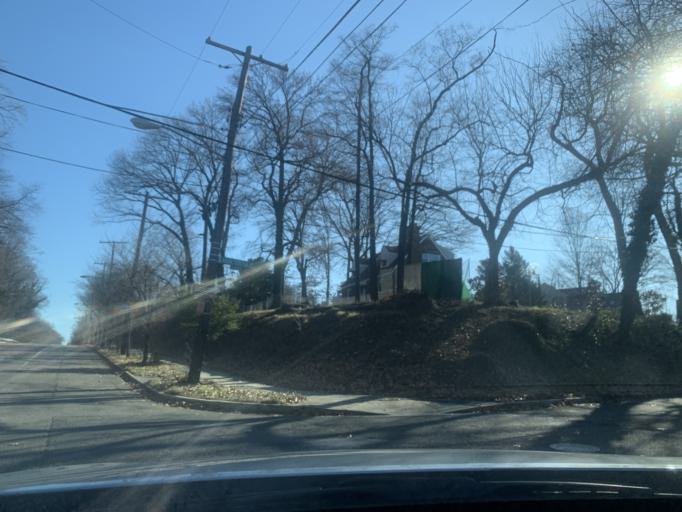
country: US
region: Maryland
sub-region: Prince George's County
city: Silver Hill
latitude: 38.8775
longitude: -76.9602
